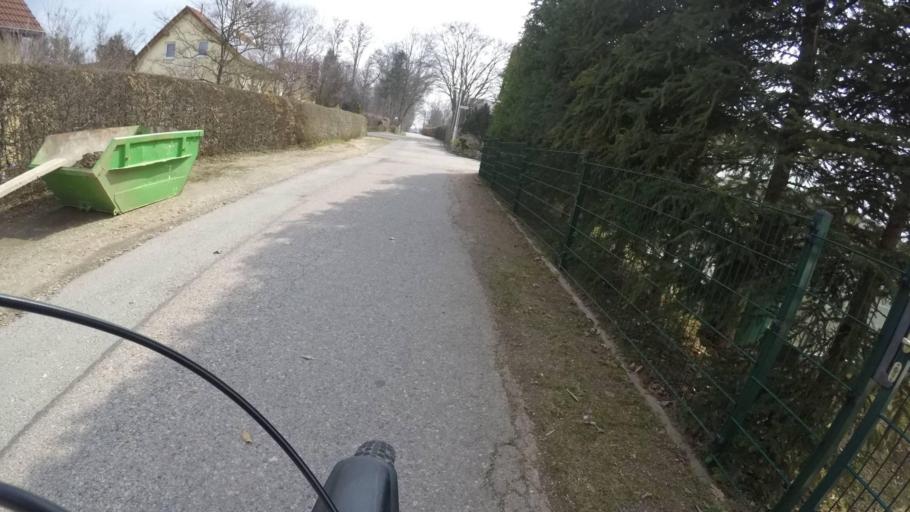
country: DE
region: Saxony
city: Limbach-Oberfrohna
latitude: 50.8550
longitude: 12.7682
